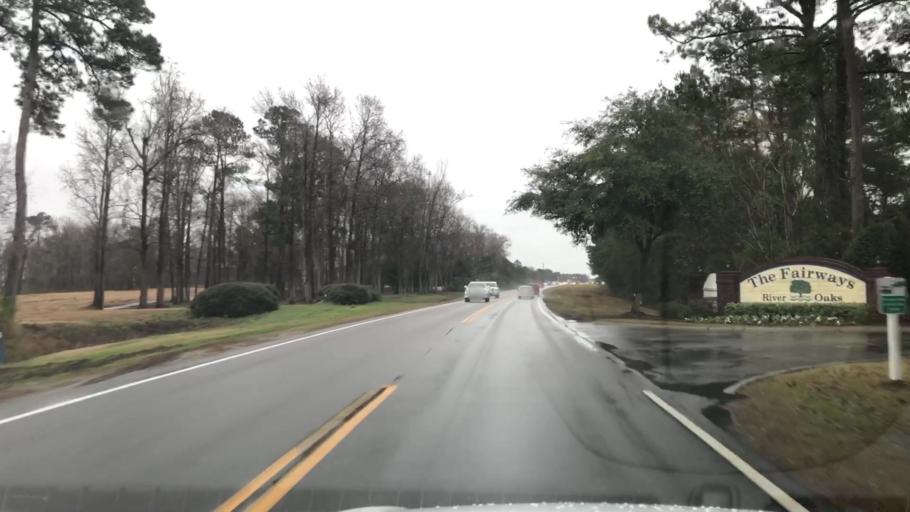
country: US
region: South Carolina
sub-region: Horry County
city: Myrtle Beach
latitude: 33.7329
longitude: -78.9047
